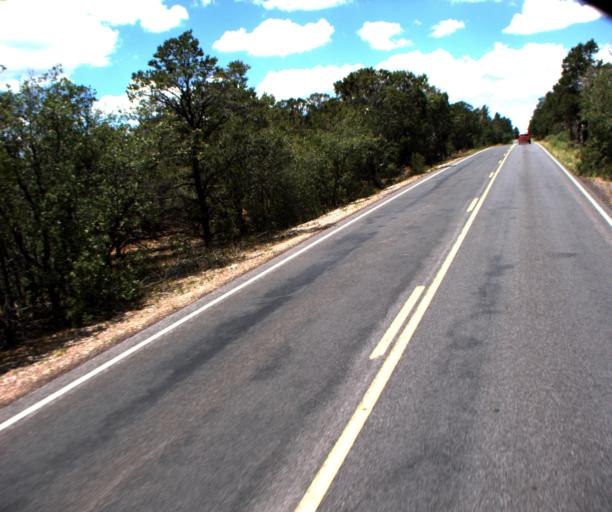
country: US
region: Arizona
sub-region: Coconino County
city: Grand Canyon
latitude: 36.0036
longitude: -112.0435
